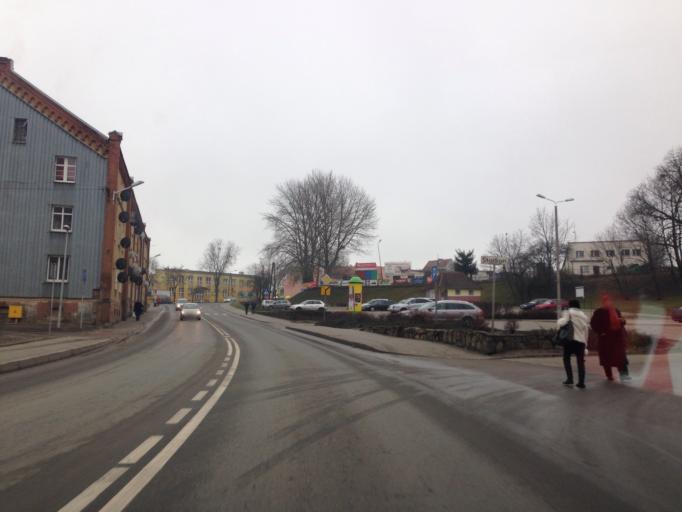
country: PL
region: Warmian-Masurian Voivodeship
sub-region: Powiat ketrzynski
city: Ketrzyn
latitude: 54.0724
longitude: 21.3746
